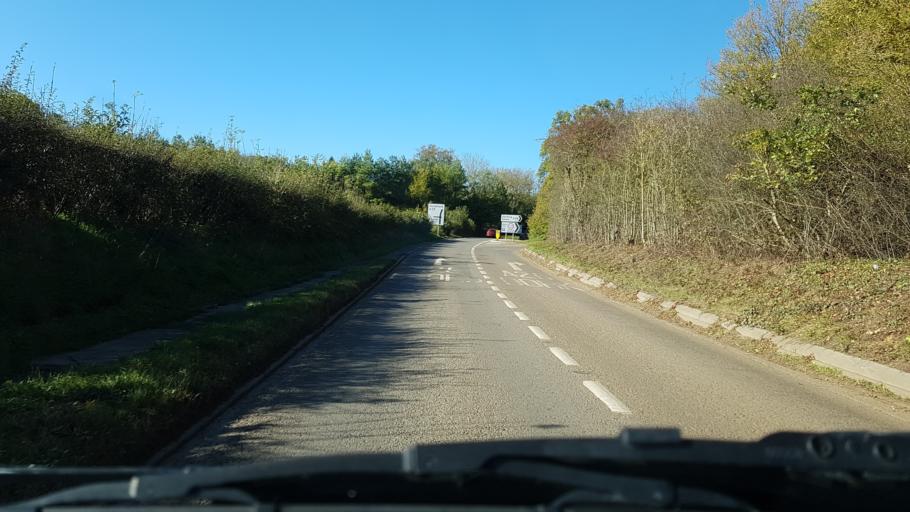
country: GB
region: England
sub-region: Surrey
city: Chilworth
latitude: 51.2254
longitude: -0.4857
